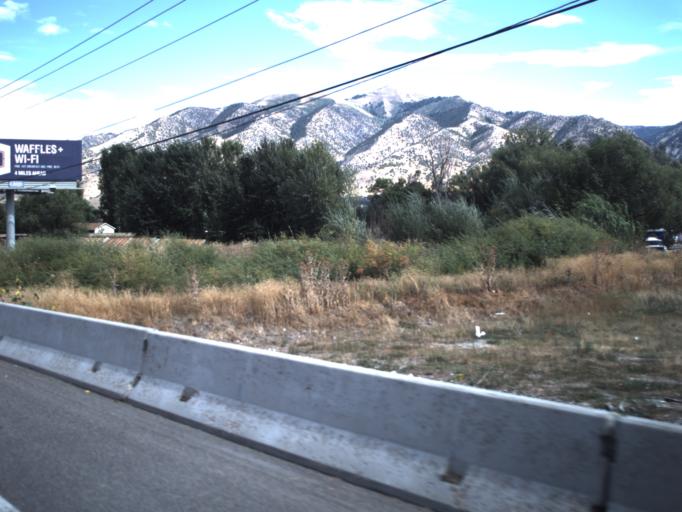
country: US
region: Utah
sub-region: Cache County
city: Providence
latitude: 41.7039
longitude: -111.8508
